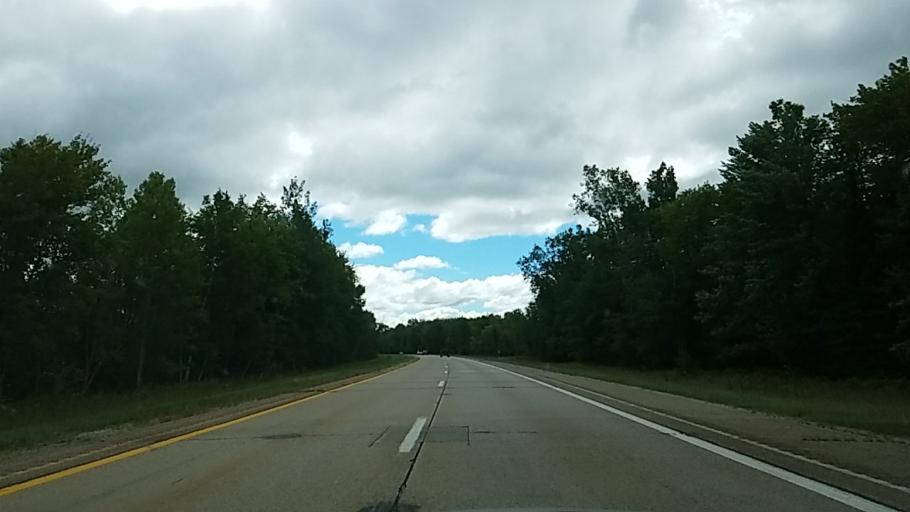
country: US
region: Michigan
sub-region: Ogemaw County
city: West Branch
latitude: 44.1927
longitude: -84.1871
